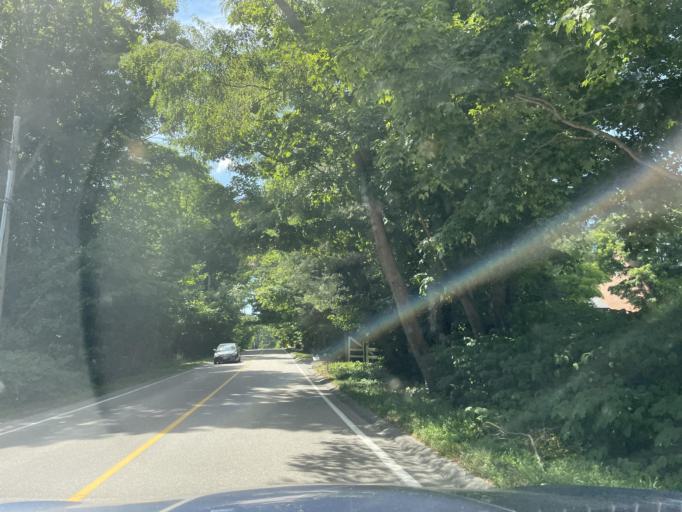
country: US
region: Massachusetts
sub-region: Middlesex County
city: Sherborn
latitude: 42.2364
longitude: -71.4021
